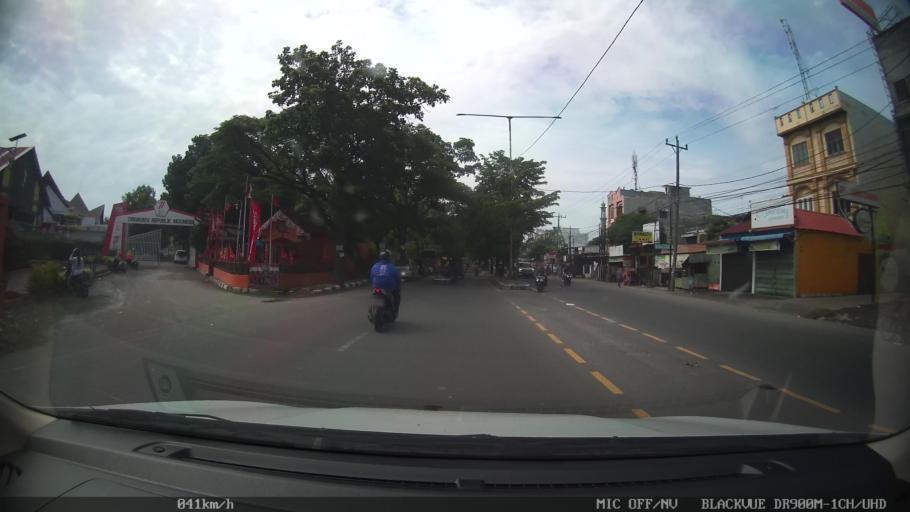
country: ID
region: North Sumatra
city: Medan
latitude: 3.6126
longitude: 98.7072
